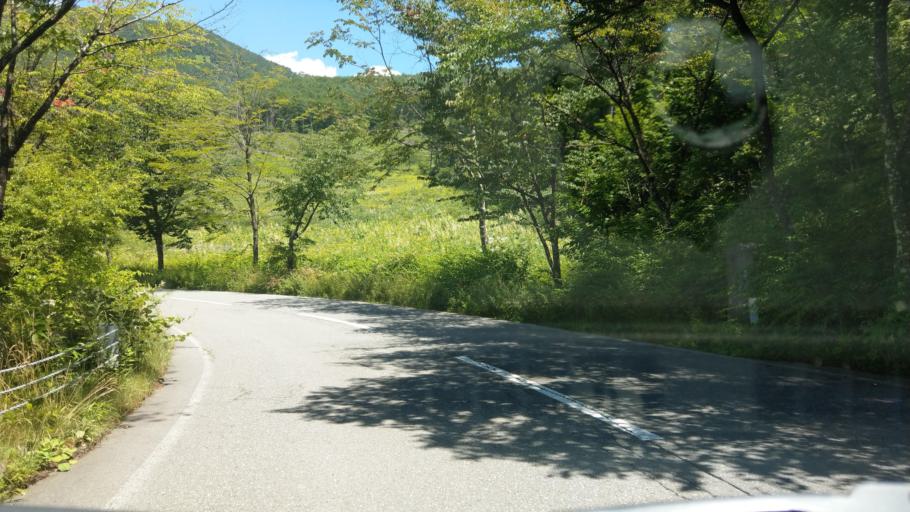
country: JP
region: Nagano
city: Komoro
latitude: 36.3846
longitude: 138.4655
